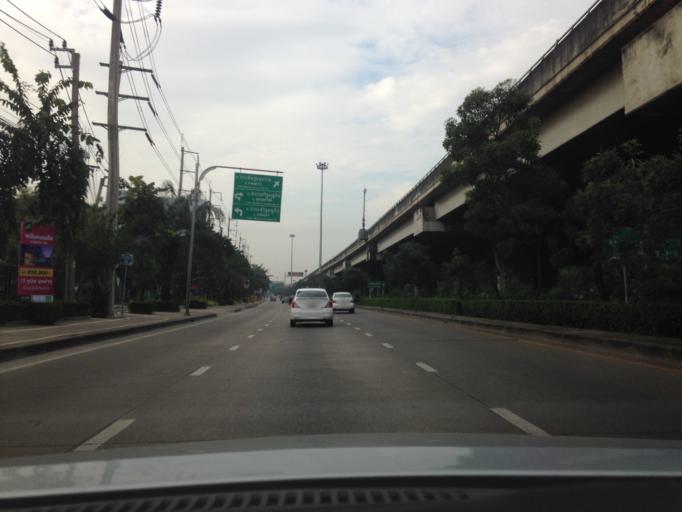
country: TH
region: Bangkok
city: Lat Phrao
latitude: 13.8324
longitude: 100.6306
